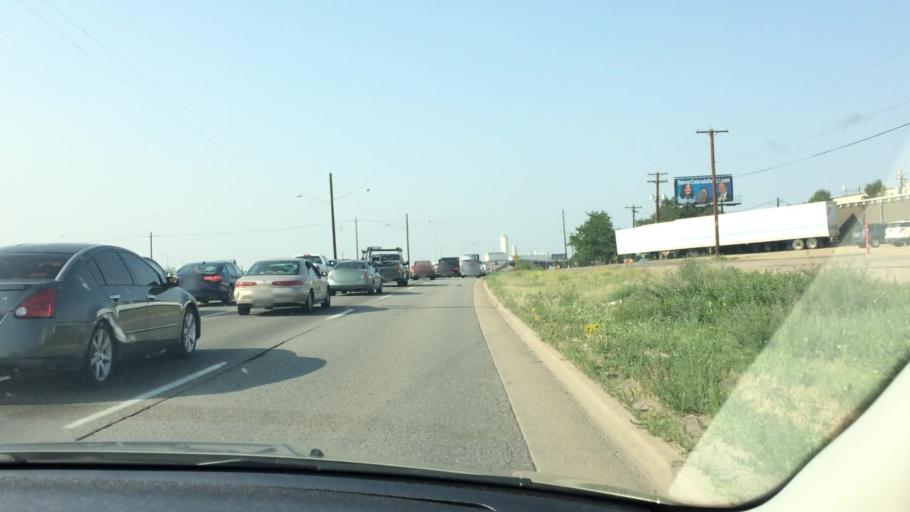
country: US
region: Colorado
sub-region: Adams County
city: Commerce City
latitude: 39.7891
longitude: -104.9403
